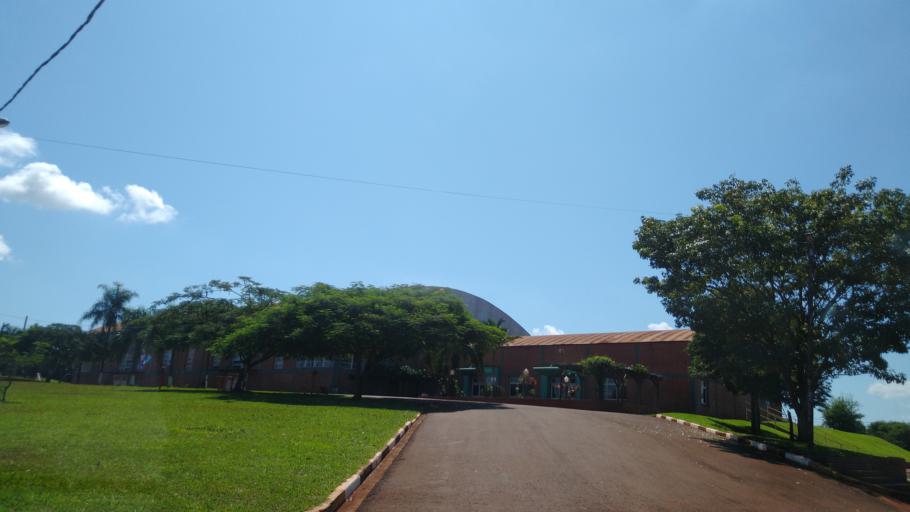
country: AR
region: Misiones
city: Puerto Libertad
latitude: -25.9659
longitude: -54.5603
